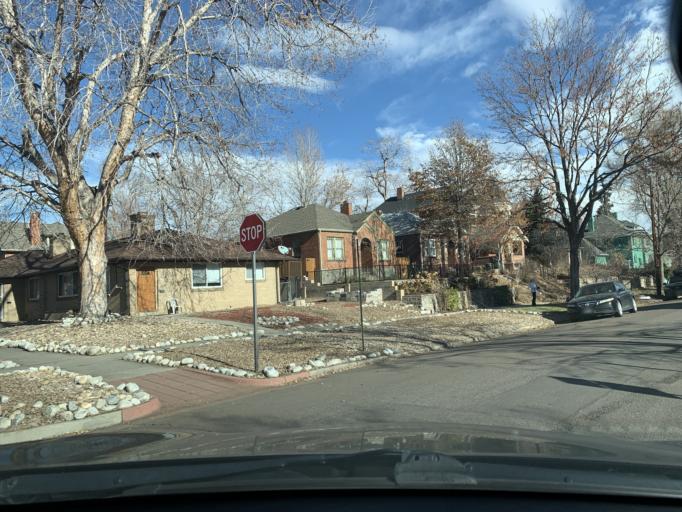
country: US
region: Colorado
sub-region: Jefferson County
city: Edgewater
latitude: 39.7524
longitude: -105.0268
